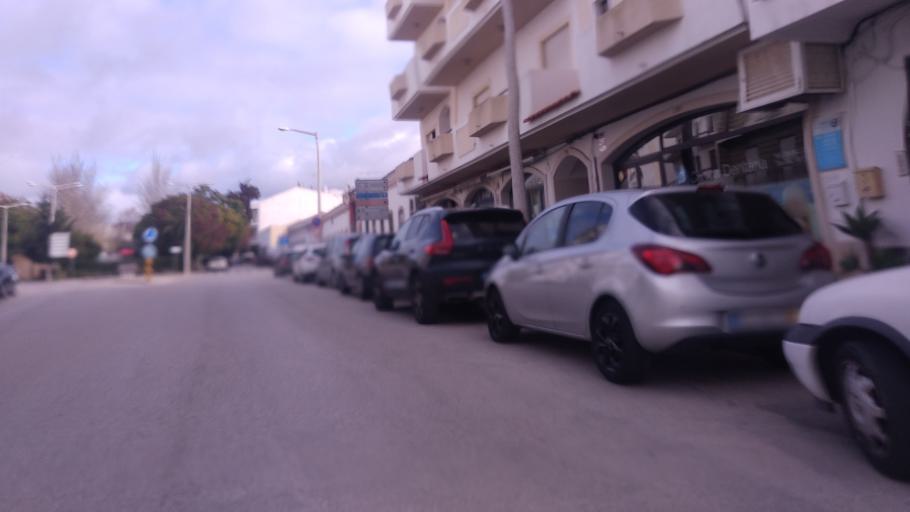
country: PT
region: Faro
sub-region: Sao Bras de Alportel
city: Sao Bras de Alportel
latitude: 37.1532
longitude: -7.8869
